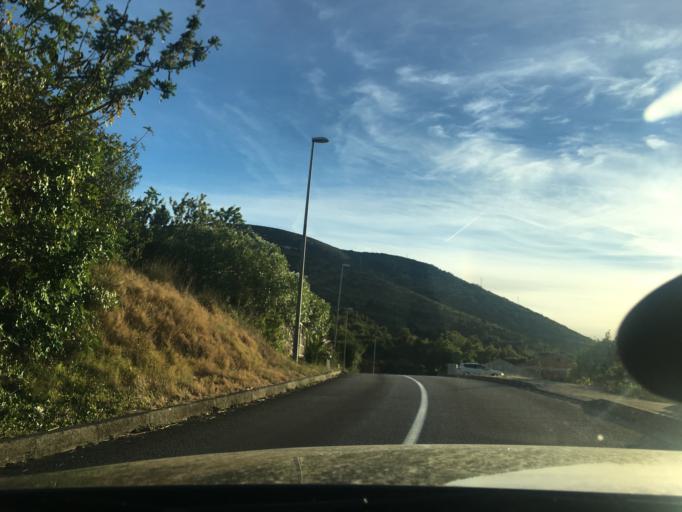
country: HR
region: Splitsko-Dalmatinska
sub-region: Grad Vis
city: Vis
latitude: 43.0562
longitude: 16.1983
